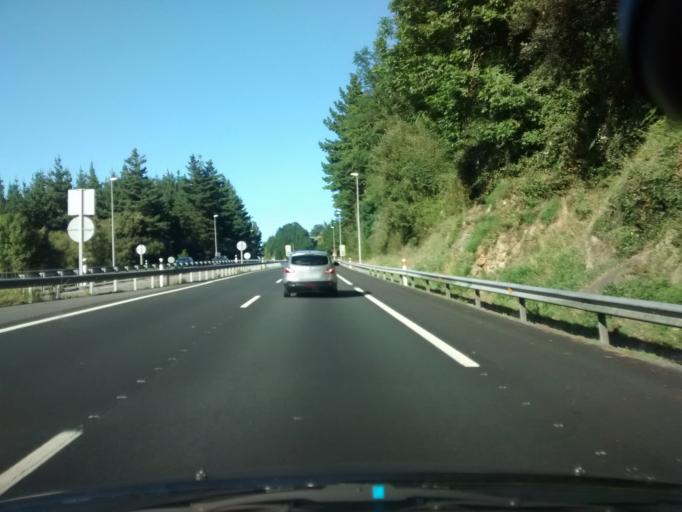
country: ES
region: Basque Country
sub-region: Provincia de Guipuzcoa
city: Deba
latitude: 43.2791
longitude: -2.3620
